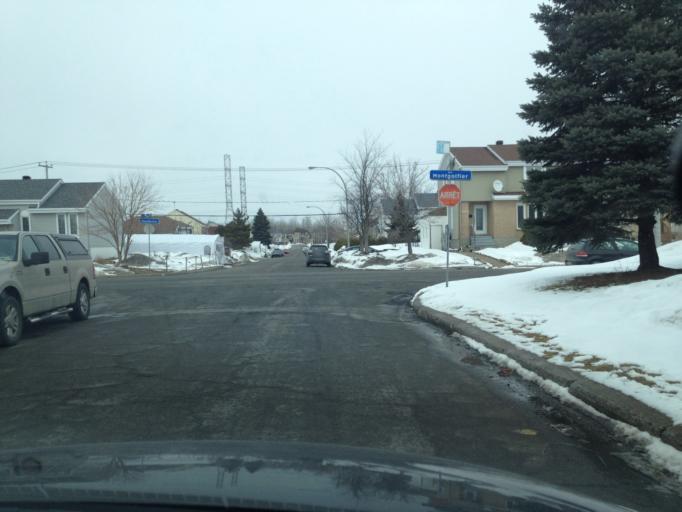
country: CA
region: Quebec
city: Dollard-Des Ormeaux
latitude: 45.5383
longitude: -73.7876
